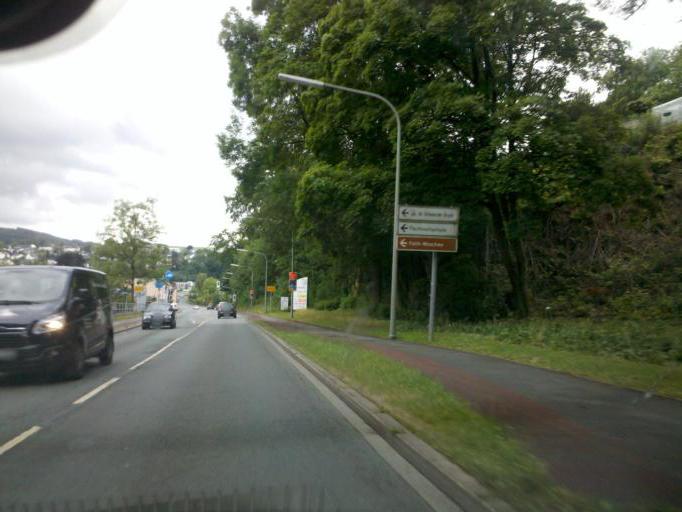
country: DE
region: North Rhine-Westphalia
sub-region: Regierungsbezirk Arnsberg
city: Meschede
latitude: 51.3541
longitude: 8.2820
